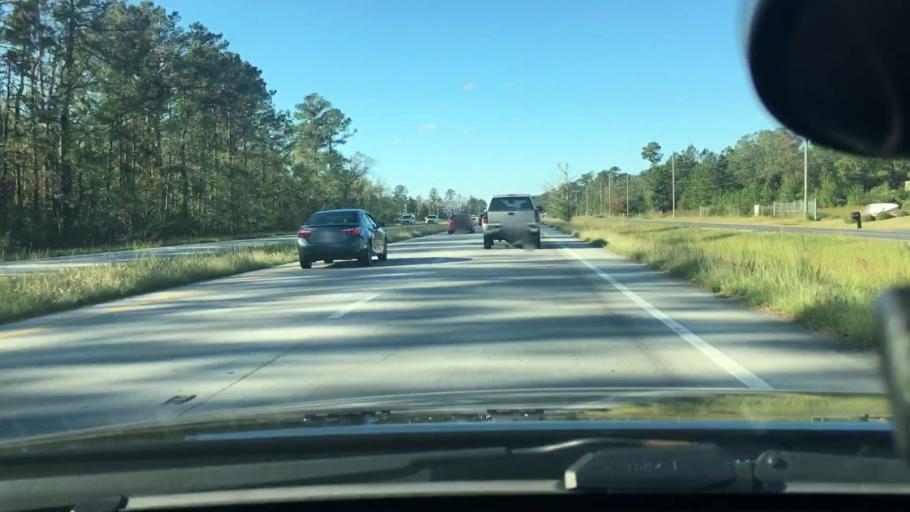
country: US
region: North Carolina
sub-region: Craven County
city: Neuse Forest
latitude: 35.0045
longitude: -76.9888
